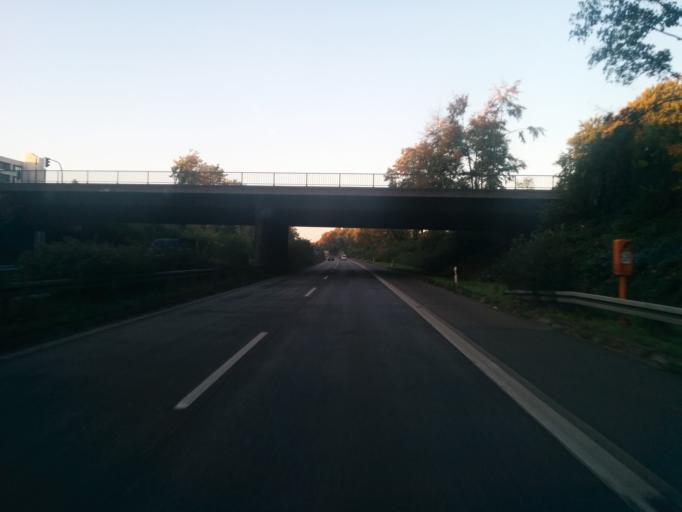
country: DE
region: North Rhine-Westphalia
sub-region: Regierungsbezirk Dusseldorf
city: Essen
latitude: 51.4196
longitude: 6.9800
